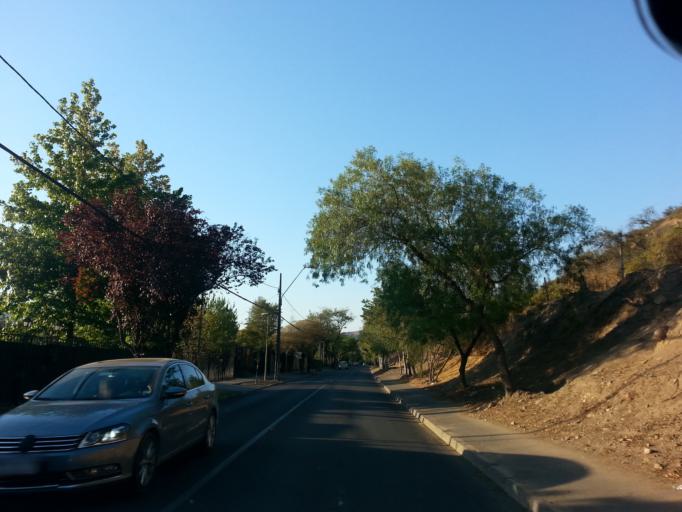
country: CL
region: Santiago Metropolitan
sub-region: Provincia de Santiago
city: Villa Presidente Frei, Nunoa, Santiago, Chile
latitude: -33.4000
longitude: -70.5401
